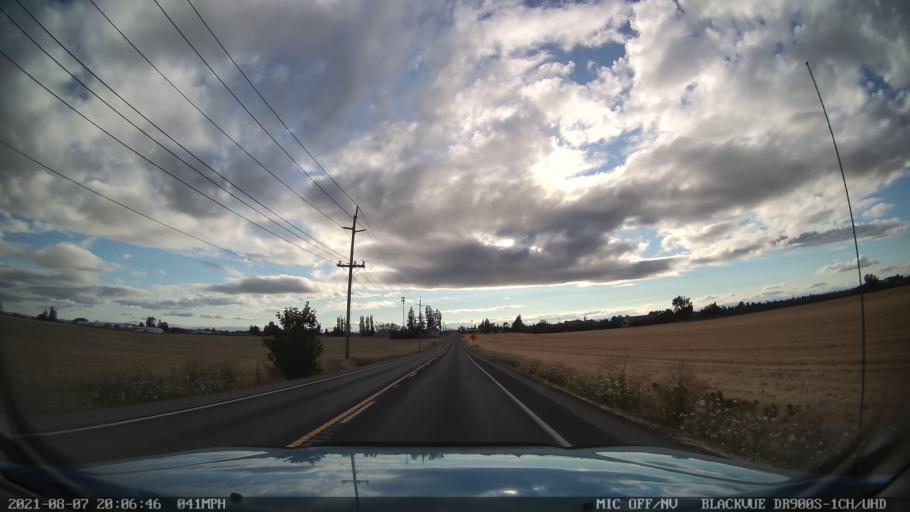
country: US
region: Oregon
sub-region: Marion County
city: Silverton
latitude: 44.9914
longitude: -122.8730
